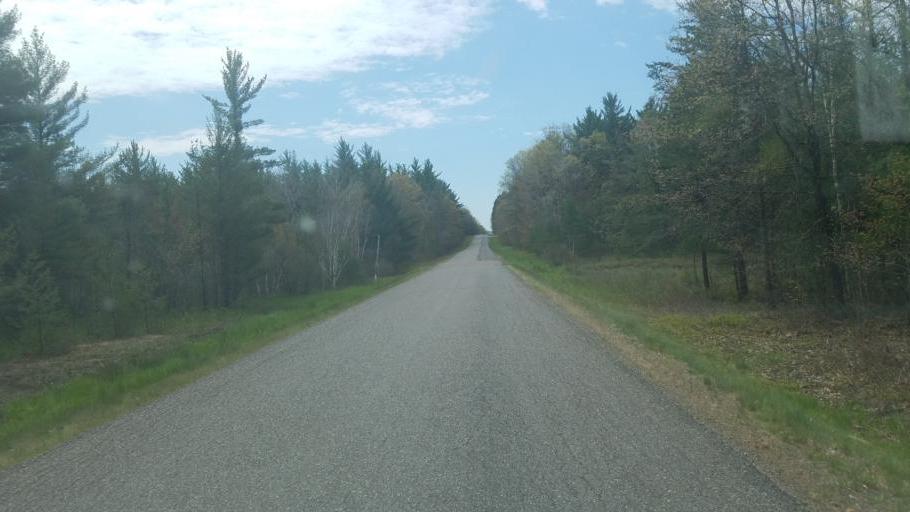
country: US
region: Wisconsin
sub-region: Clark County
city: Neillsville
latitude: 44.4181
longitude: -90.4973
